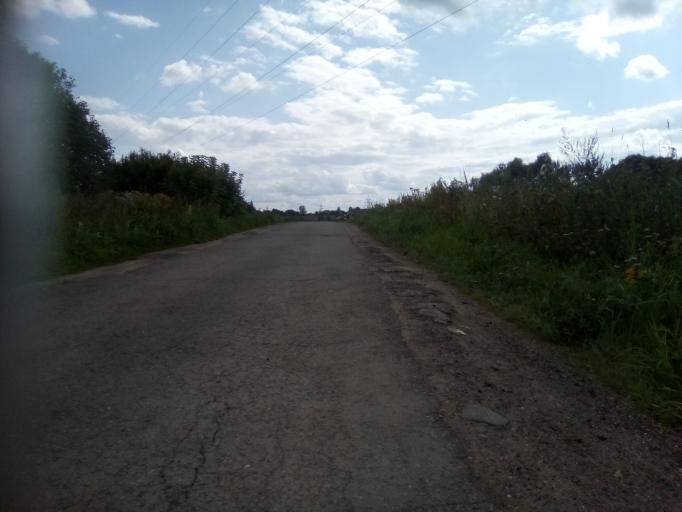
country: RU
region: Moskovskaya
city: Zhavoronki
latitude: 55.6624
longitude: 37.1358
